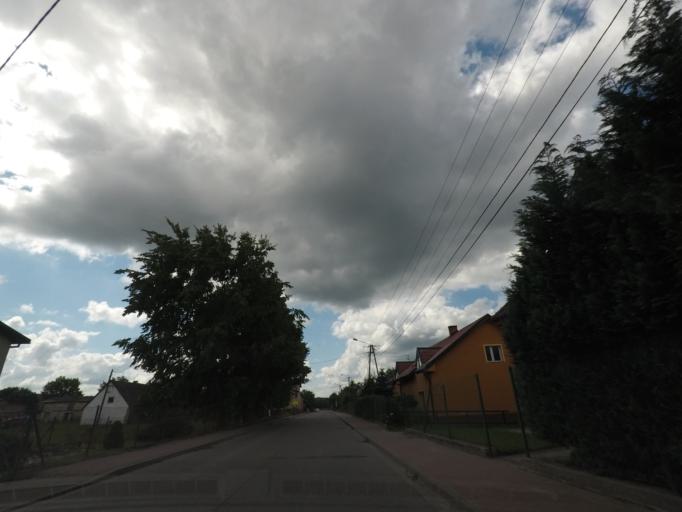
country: PL
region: Pomeranian Voivodeship
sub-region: Powiat wejherowski
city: Leczyce
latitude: 54.5894
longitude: 17.8620
